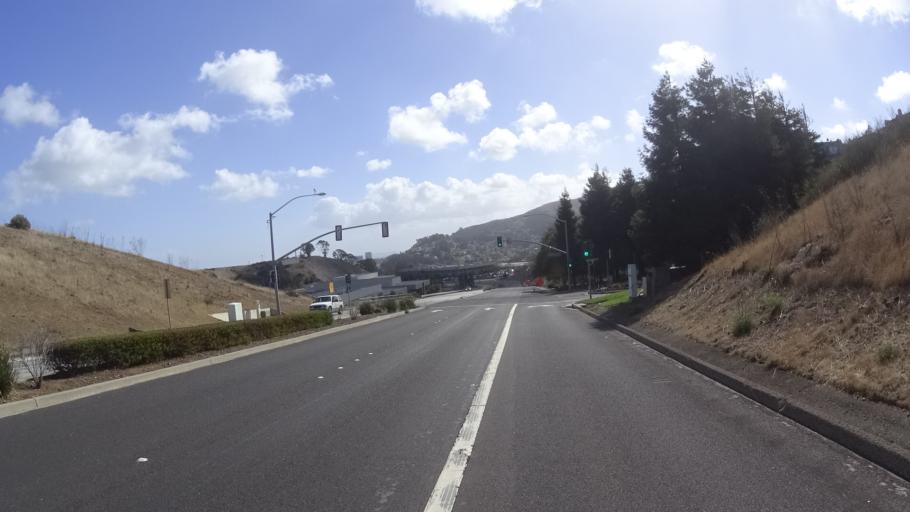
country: US
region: California
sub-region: San Mateo County
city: Brisbane
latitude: 37.6959
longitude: -122.4087
